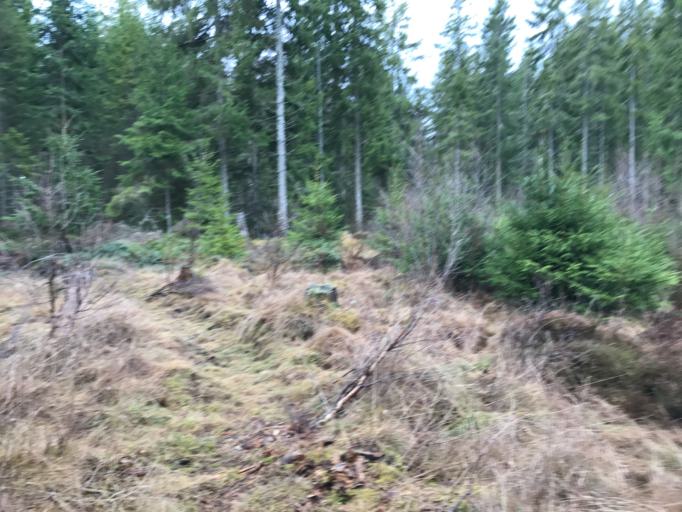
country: SE
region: Kronoberg
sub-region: Vaxjo Kommun
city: Braas
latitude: 56.9235
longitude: 15.0211
